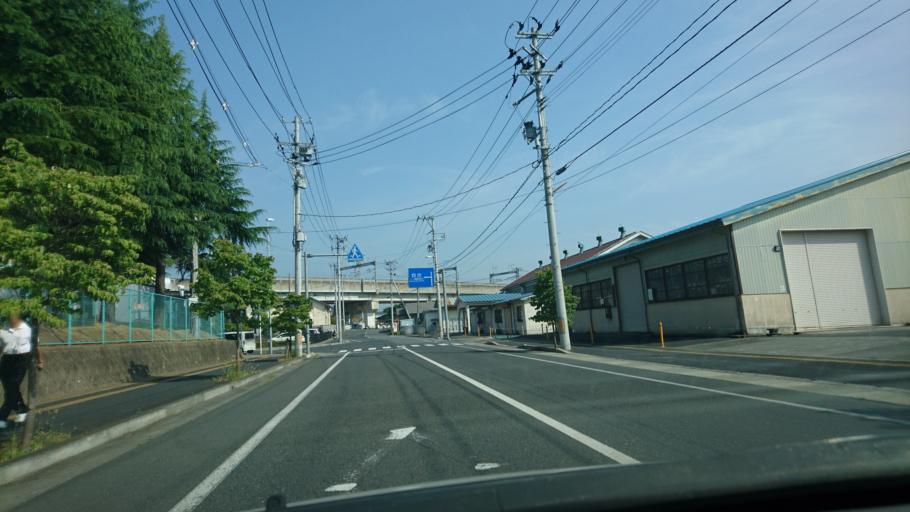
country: JP
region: Iwate
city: Ichinoseki
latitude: 38.9274
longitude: 141.1414
